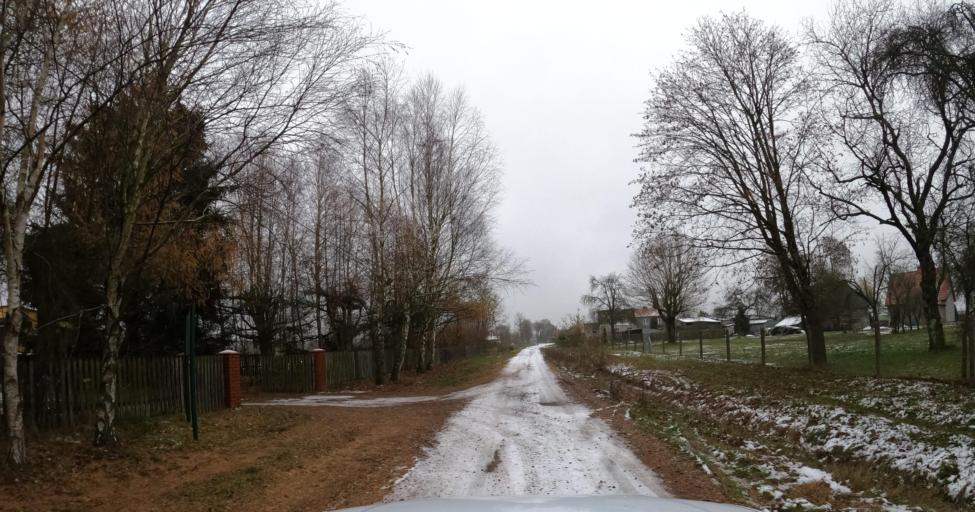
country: PL
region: West Pomeranian Voivodeship
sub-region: Powiat bialogardzki
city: Bialogard
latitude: 54.0829
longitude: 16.0868
